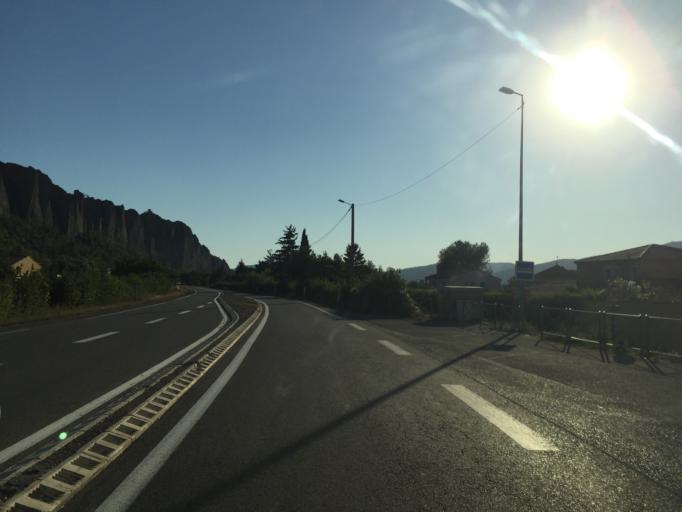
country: FR
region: Provence-Alpes-Cote d'Azur
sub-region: Departement des Alpes-de-Haute-Provence
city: Les Mees
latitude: 44.0370
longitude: 5.9916
